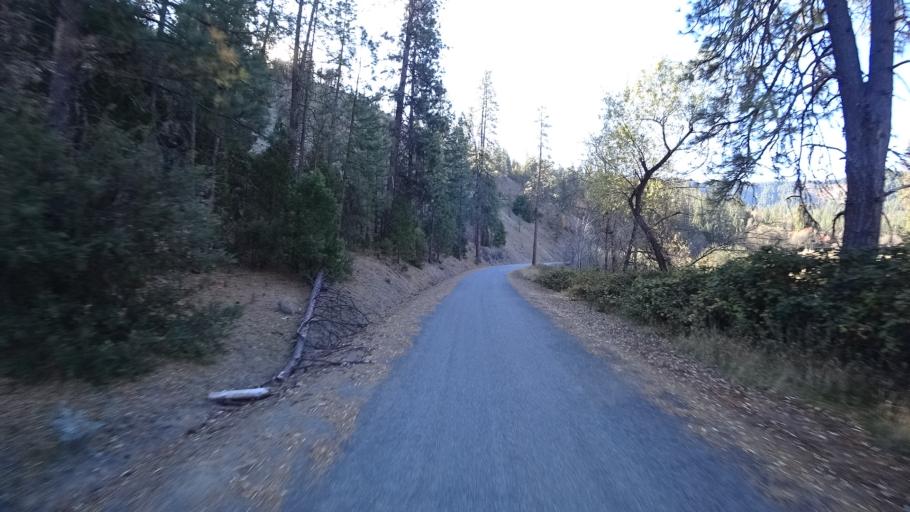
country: US
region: California
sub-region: Siskiyou County
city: Yreka
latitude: 41.8239
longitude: -122.9608
